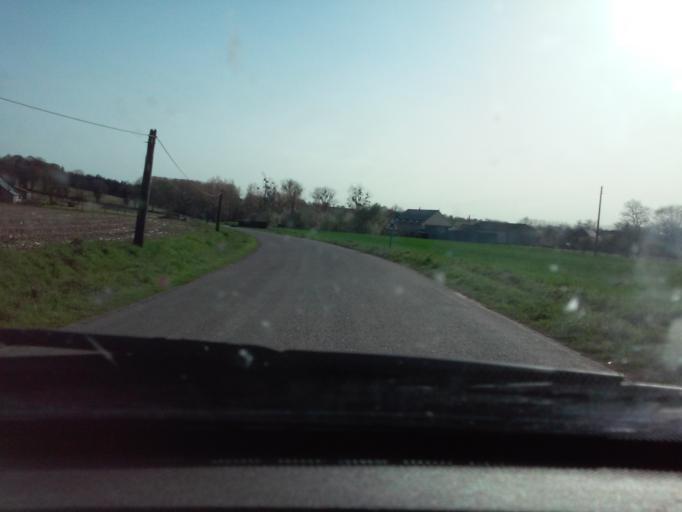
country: FR
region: Brittany
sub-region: Departement d'Ille-et-Vilaine
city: Javene
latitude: 48.3169
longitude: -1.2409
